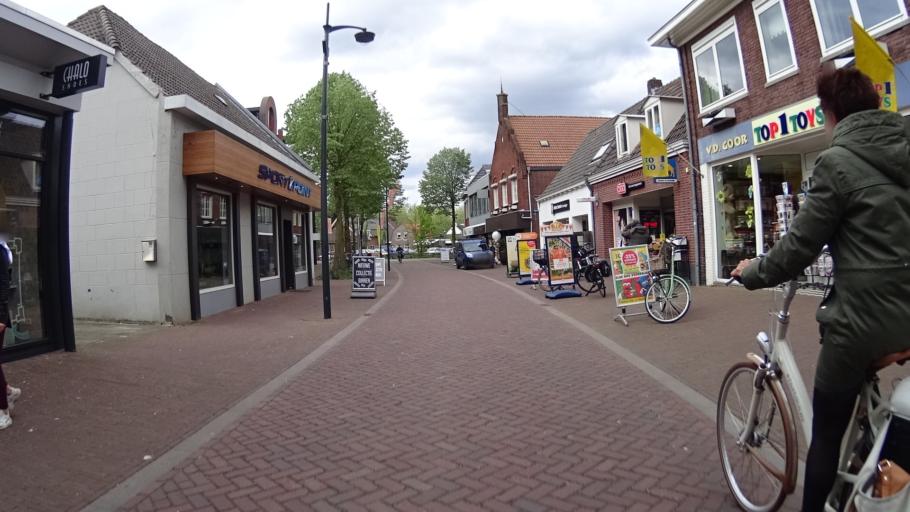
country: NL
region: North Brabant
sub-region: Gemeente Boekel
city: Boekel
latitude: 51.5576
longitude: 5.6823
